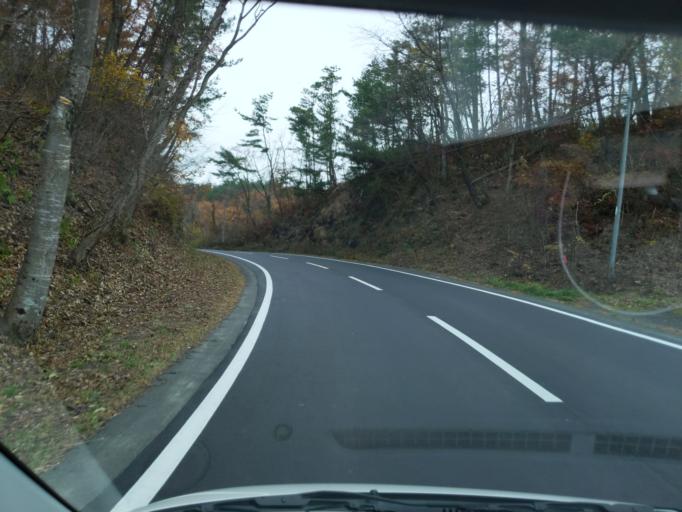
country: JP
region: Iwate
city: Kitakami
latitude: 39.2400
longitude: 141.2177
